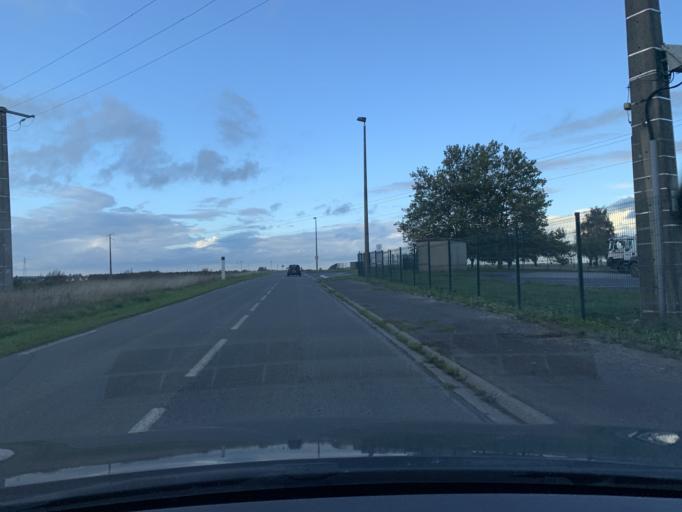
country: FR
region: Nord-Pas-de-Calais
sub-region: Departement du Nord
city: Proville
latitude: 50.1479
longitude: 3.2105
